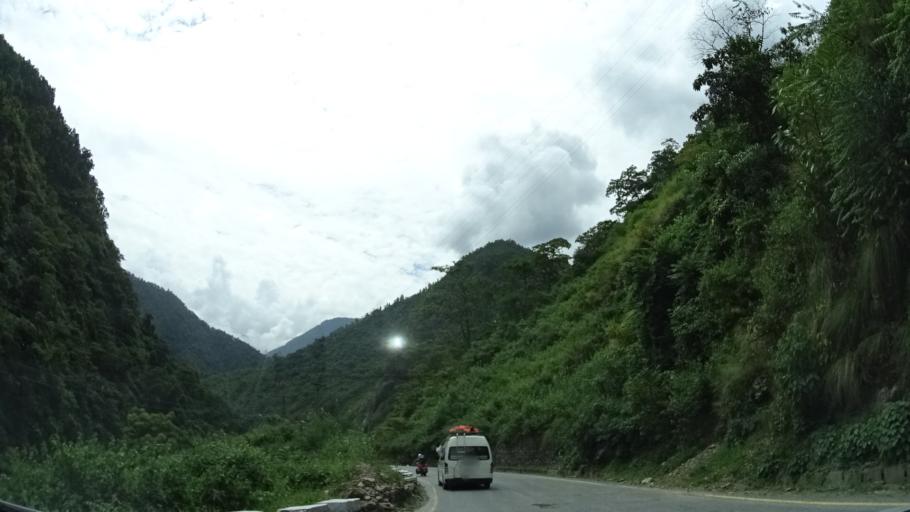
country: NP
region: Central Region
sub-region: Narayani Zone
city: Bharatpur
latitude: 27.8897
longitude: 84.5398
